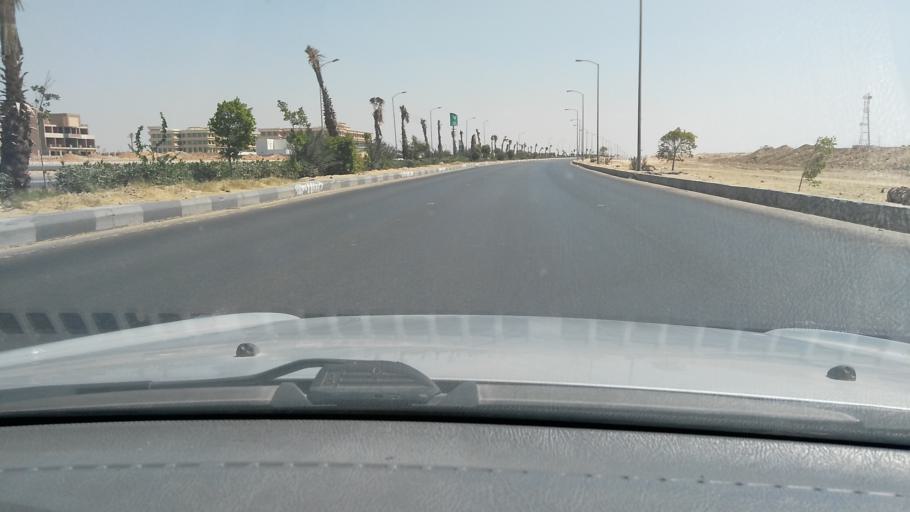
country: EG
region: Al Jizah
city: Madinat Sittah Uktubar
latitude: 29.9509
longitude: 30.9535
